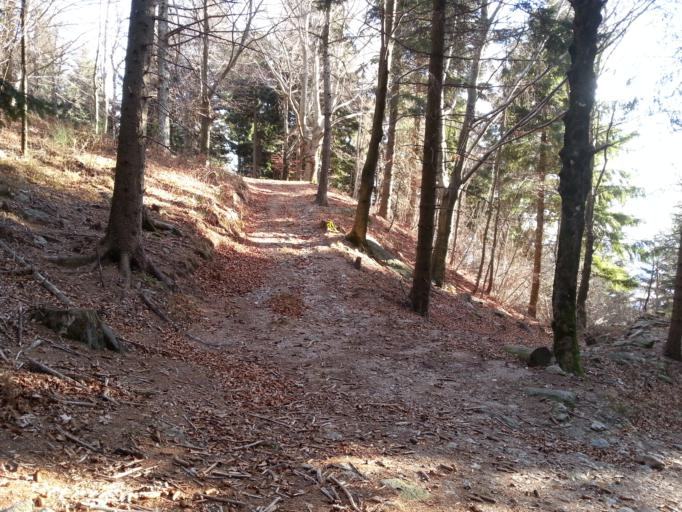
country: CH
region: Ticino
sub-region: Lugano District
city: Gravesano
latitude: 46.0431
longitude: 8.8635
